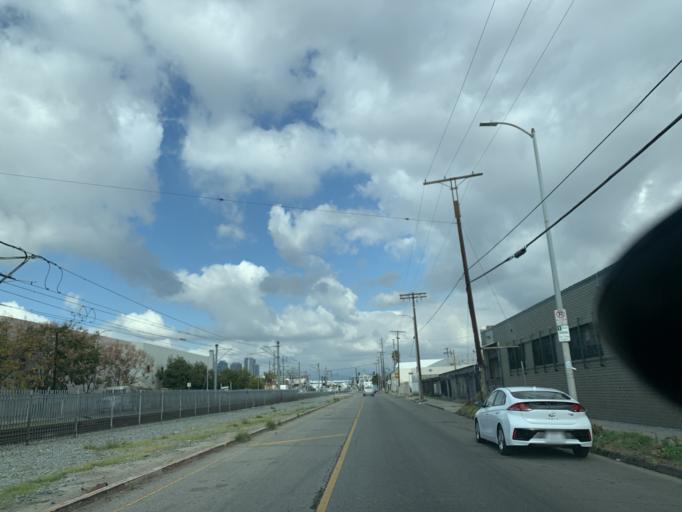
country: US
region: California
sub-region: Los Angeles County
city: Los Angeles
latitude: 34.0167
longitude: -118.2429
